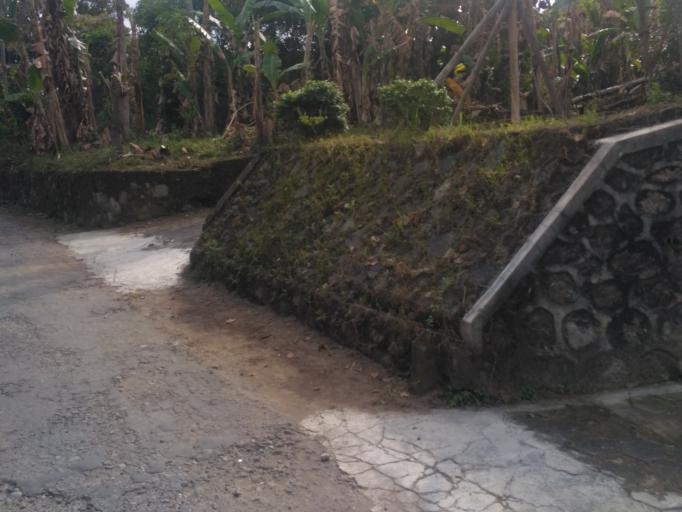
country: ID
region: Daerah Istimewa Yogyakarta
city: Melati
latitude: -7.7537
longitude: 110.3687
